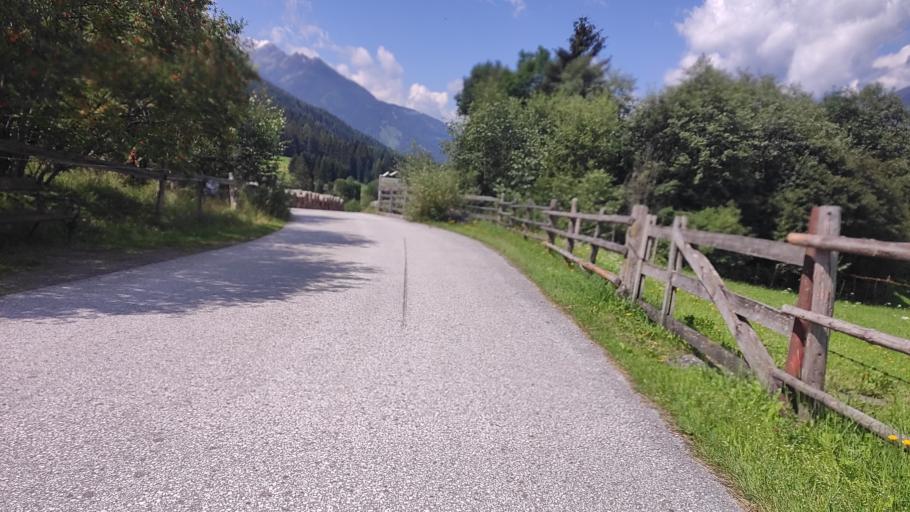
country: AT
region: Salzburg
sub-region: Politischer Bezirk Zell am See
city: Neukirchen am Grossvenediger
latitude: 47.2511
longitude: 12.3057
